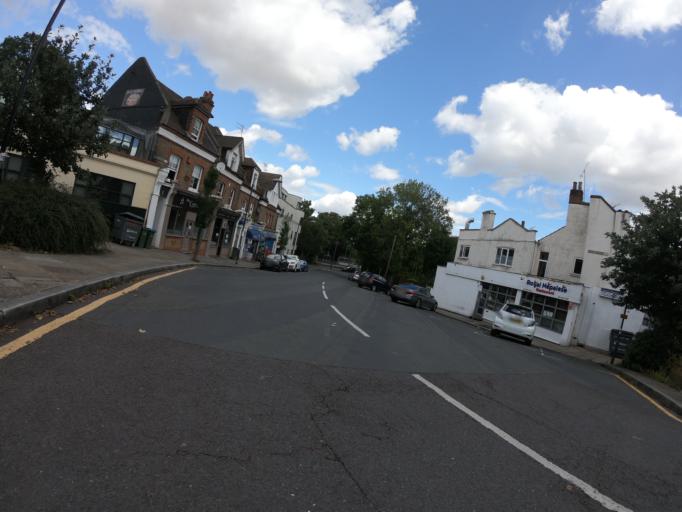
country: GB
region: England
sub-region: Greater London
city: Blackheath
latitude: 51.4835
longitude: 0.0173
